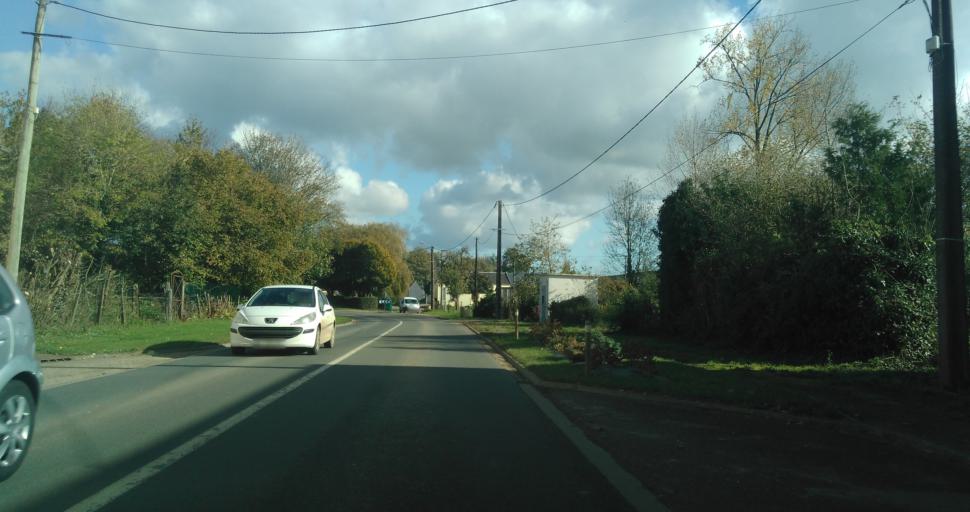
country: FR
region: Picardie
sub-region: Departement de la Somme
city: Doullens
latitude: 50.1528
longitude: 2.2830
